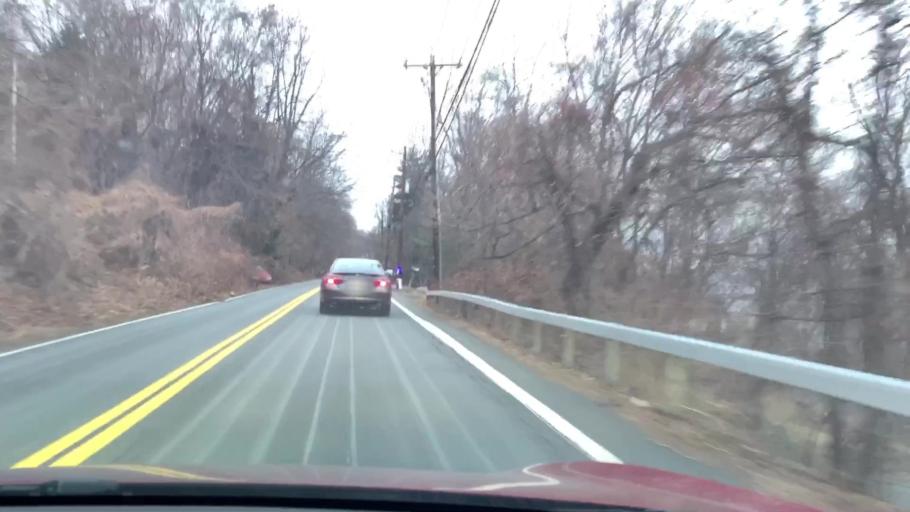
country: US
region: New York
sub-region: Rockland County
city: Piermont
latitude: 41.0452
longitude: -73.9213
